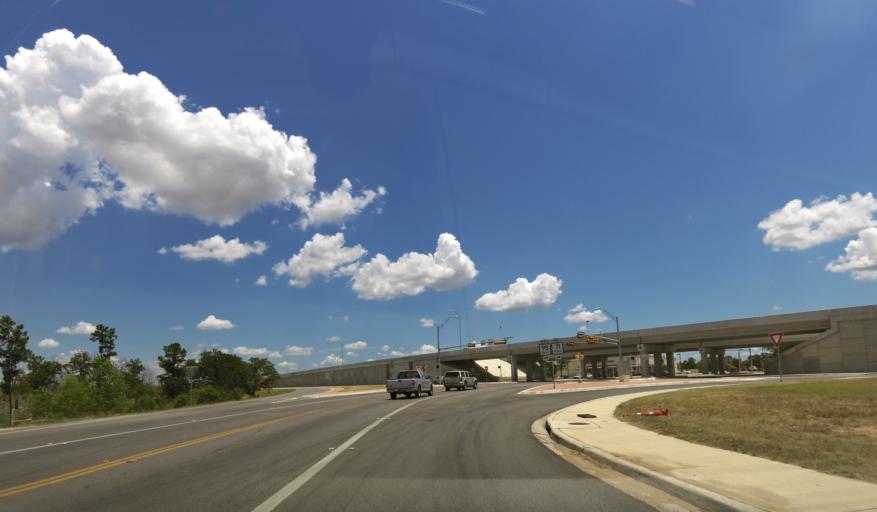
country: US
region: Texas
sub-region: Bastrop County
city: Bastrop
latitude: 30.1032
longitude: -97.2846
